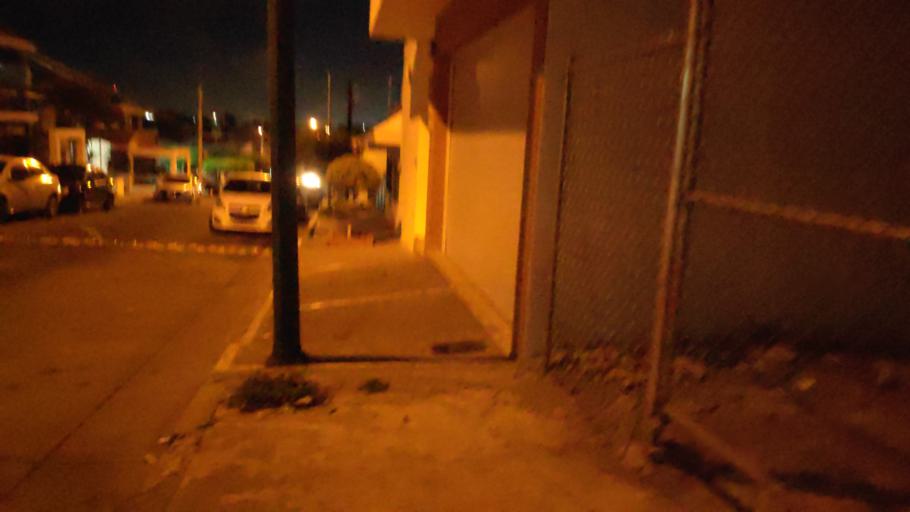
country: MX
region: Sinaloa
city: Culiacan
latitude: 24.7924
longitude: -107.4080
